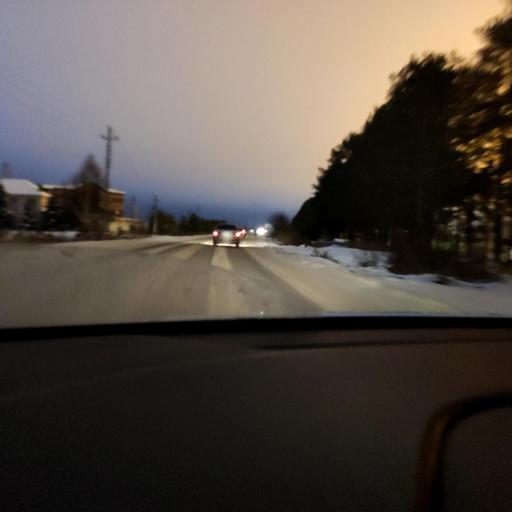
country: RU
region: Tatarstan
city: Osinovo
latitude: 55.8842
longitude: 48.8881
